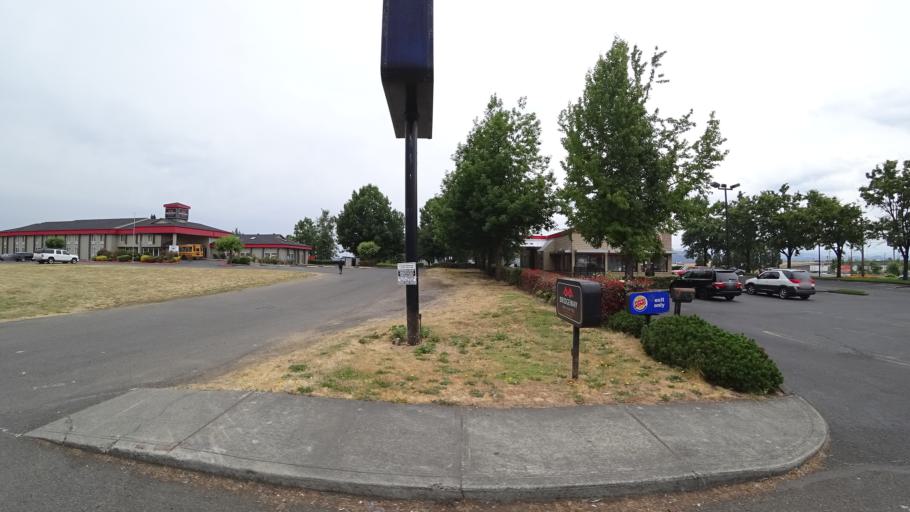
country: US
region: Oregon
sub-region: Multnomah County
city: Fairview
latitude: 45.5394
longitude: -122.4781
